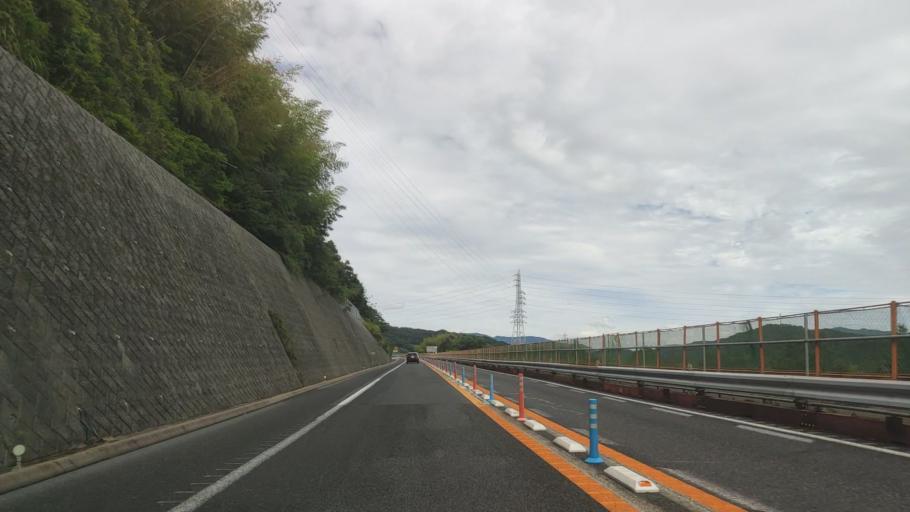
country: JP
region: Wakayama
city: Gobo
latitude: 33.8345
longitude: 135.2202
